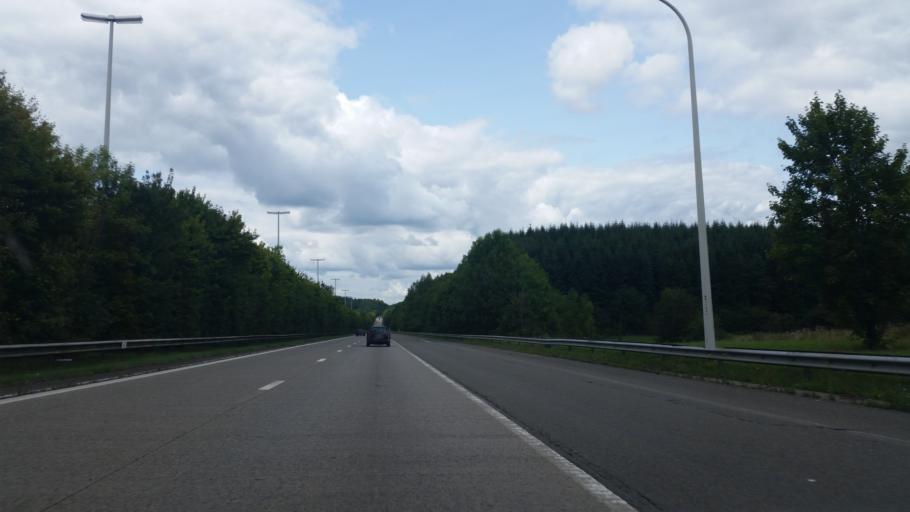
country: BE
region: Wallonia
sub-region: Province de Namur
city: Ciney
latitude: 50.2707
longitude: 5.0328
